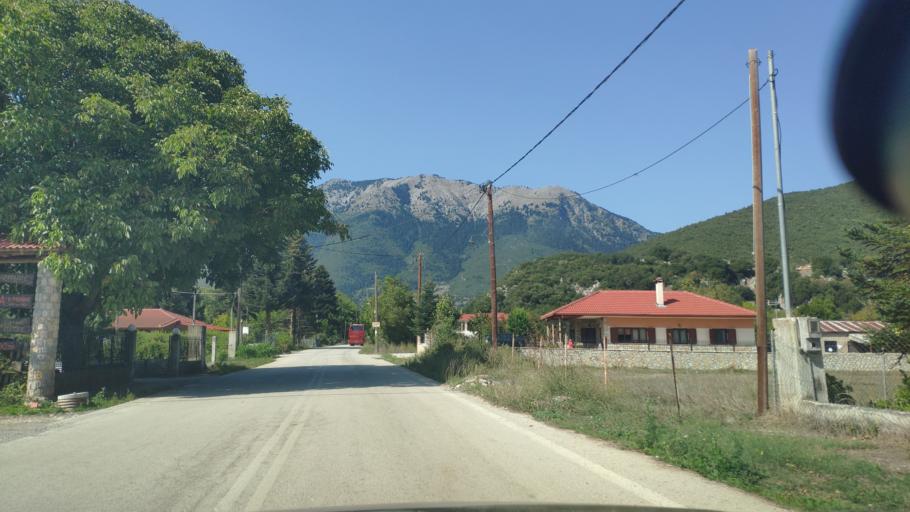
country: GR
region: Peloponnese
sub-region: Nomos Korinthias
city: Nemea
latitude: 37.8453
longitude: 22.4124
